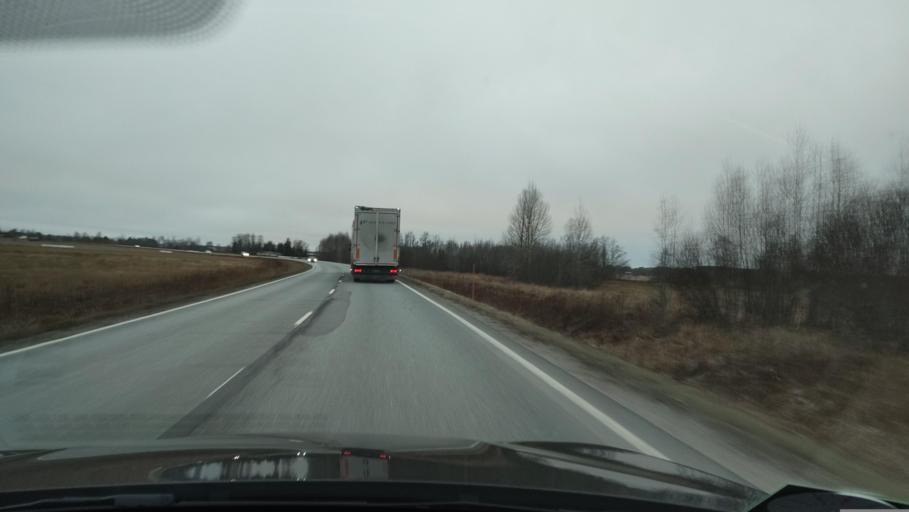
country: FI
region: Southern Ostrobothnia
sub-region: Suupohja
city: Kauhajoki
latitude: 62.3788
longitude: 22.0940
